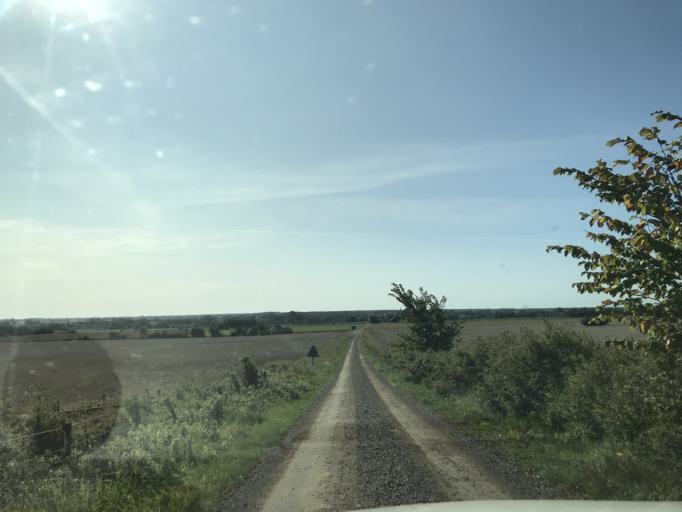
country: SE
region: Skane
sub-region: Landskrona
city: Asmundtorp
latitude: 55.9019
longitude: 12.9491
